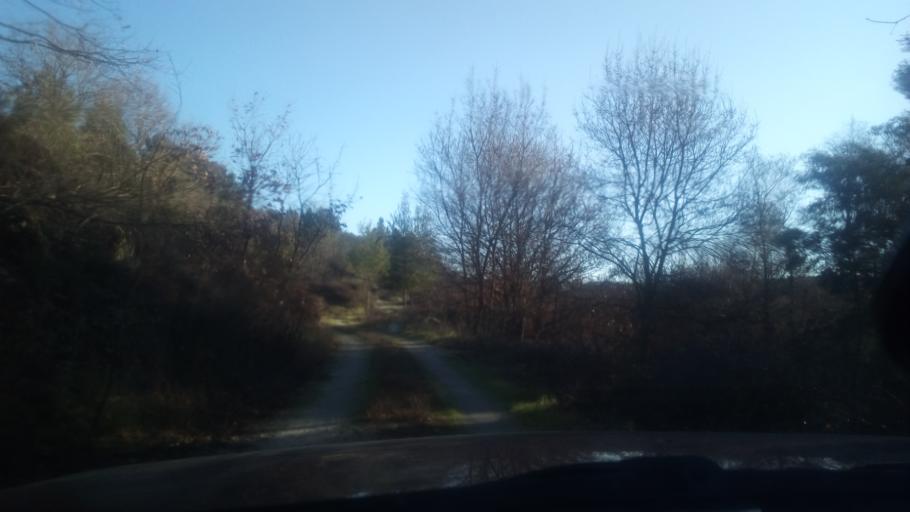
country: PT
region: Guarda
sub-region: Fornos de Algodres
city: Fornos de Algodres
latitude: 40.6064
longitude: -7.5339
